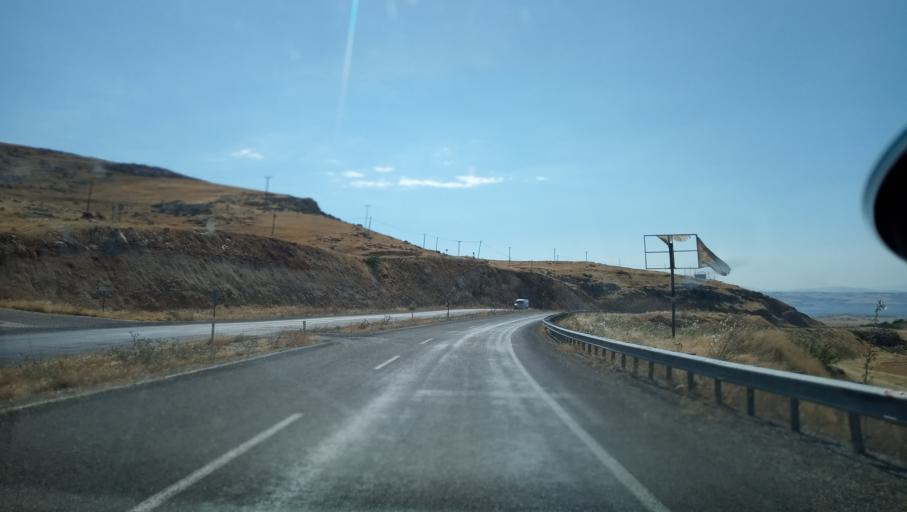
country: TR
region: Diyarbakir
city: Silvan
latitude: 38.1277
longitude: 41.0877
